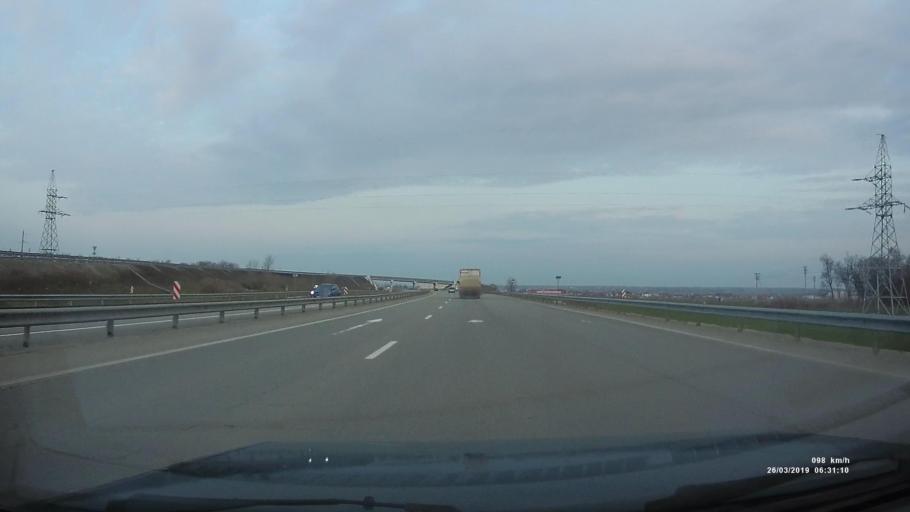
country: RU
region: Rostov
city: Krym
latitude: 47.2731
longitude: 39.5375
